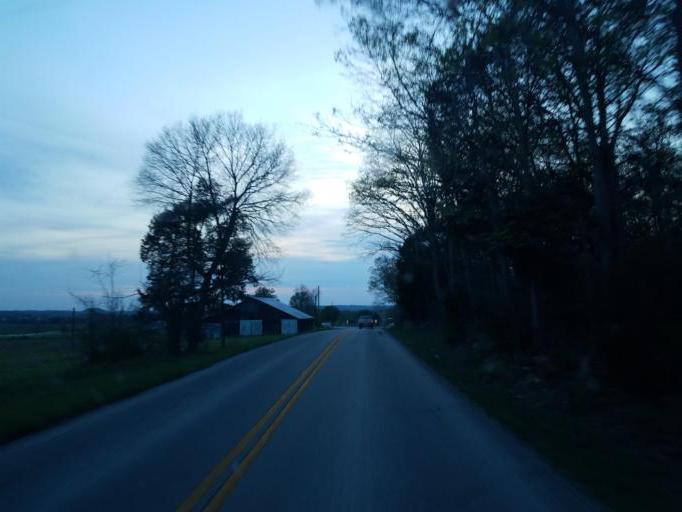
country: US
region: Kentucky
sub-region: Hart County
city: Munfordville
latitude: 37.2739
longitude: -85.8270
